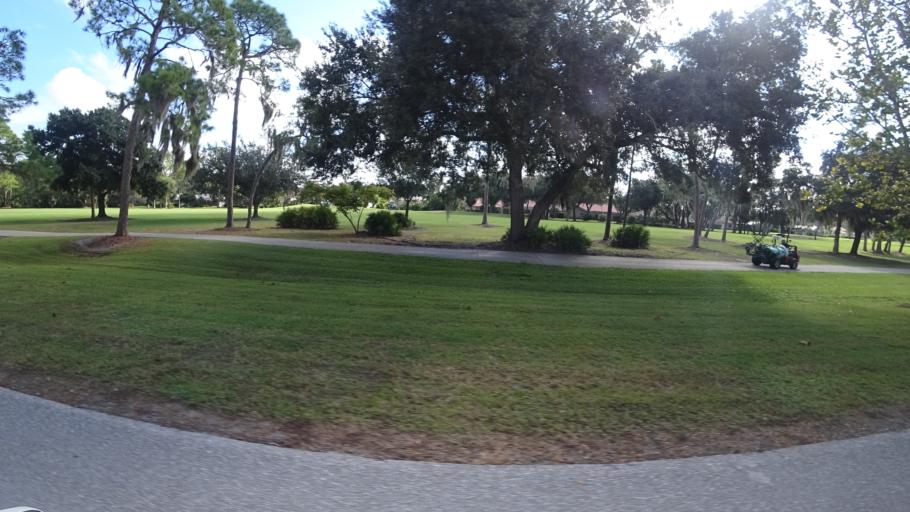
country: US
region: Florida
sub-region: Sarasota County
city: Desoto Lakes
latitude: 27.4010
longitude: -82.4871
